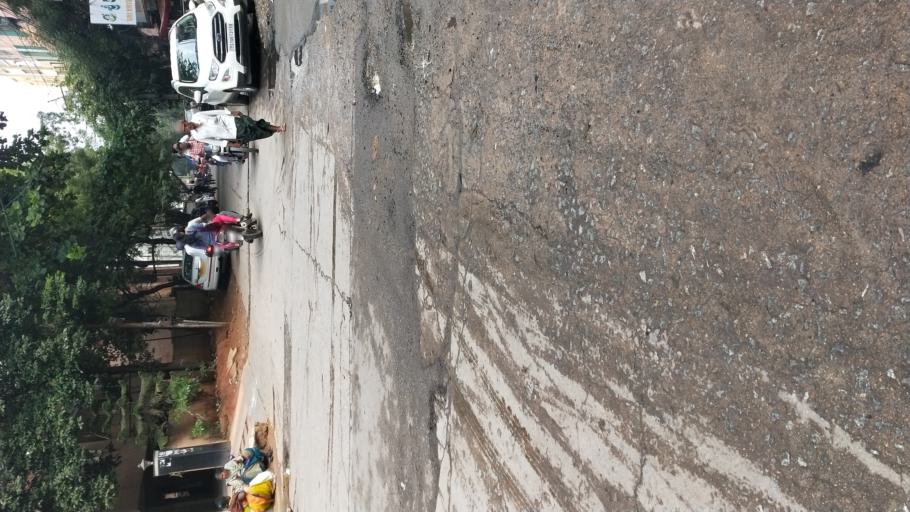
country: IN
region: Telangana
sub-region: Rangareddi
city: Kukatpalli
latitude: 17.4946
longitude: 78.4031
